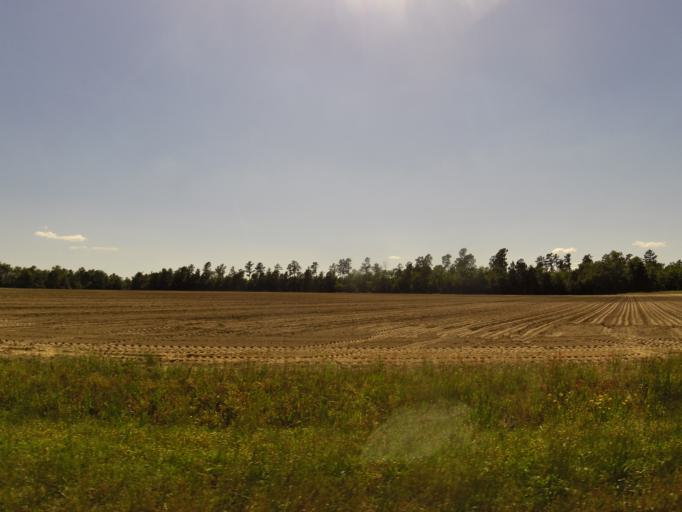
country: US
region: South Carolina
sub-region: Barnwell County
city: Williston
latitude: 33.4423
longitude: -81.4881
